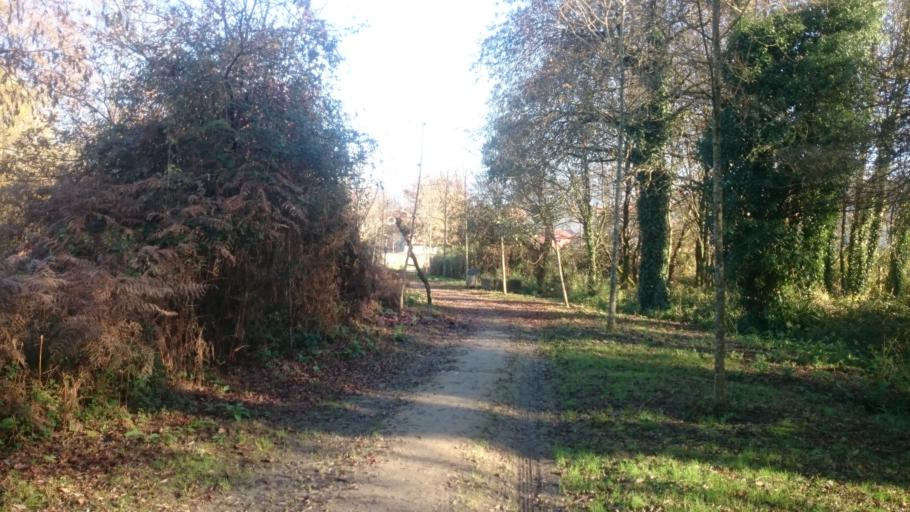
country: ES
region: Galicia
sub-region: Provincia de Pontevedra
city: Porrino
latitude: 42.1556
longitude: -8.6239
